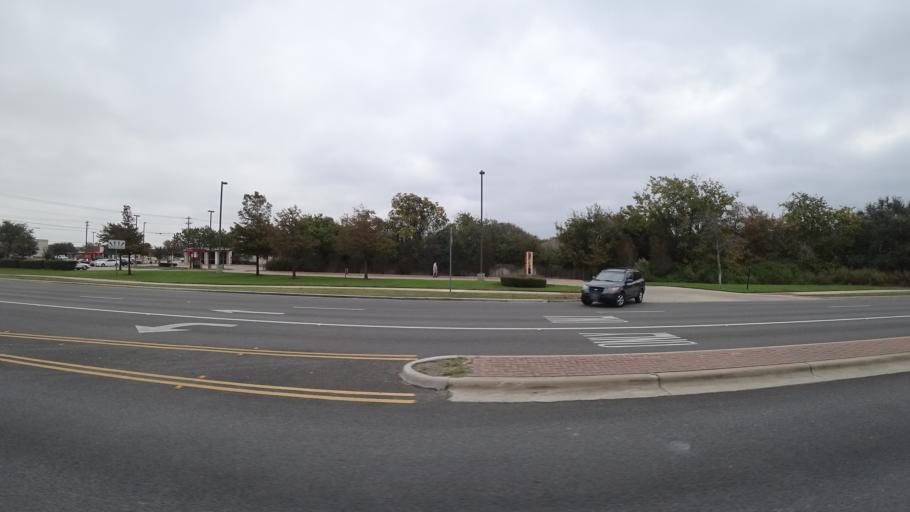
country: US
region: Texas
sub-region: Williamson County
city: Cedar Park
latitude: 30.5136
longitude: -97.8508
